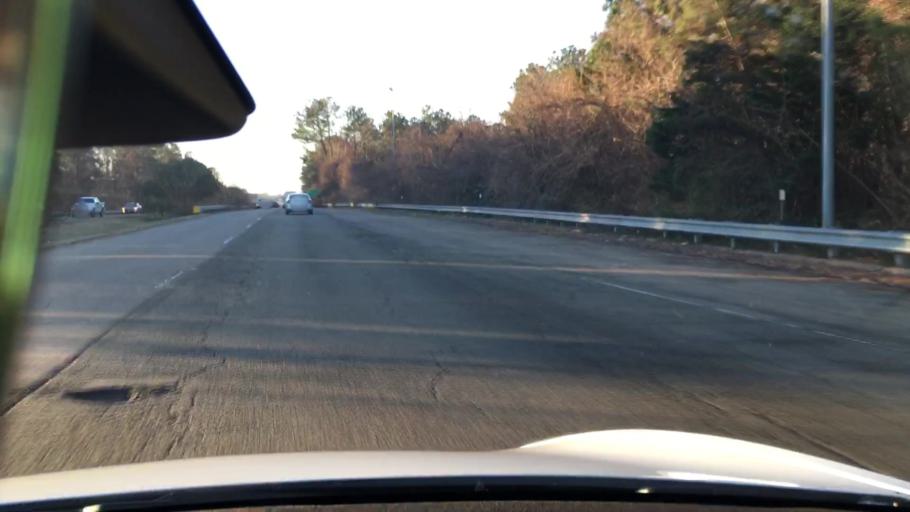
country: US
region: Virginia
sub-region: Chesterfield County
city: Bon Air
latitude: 37.5334
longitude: -77.5290
